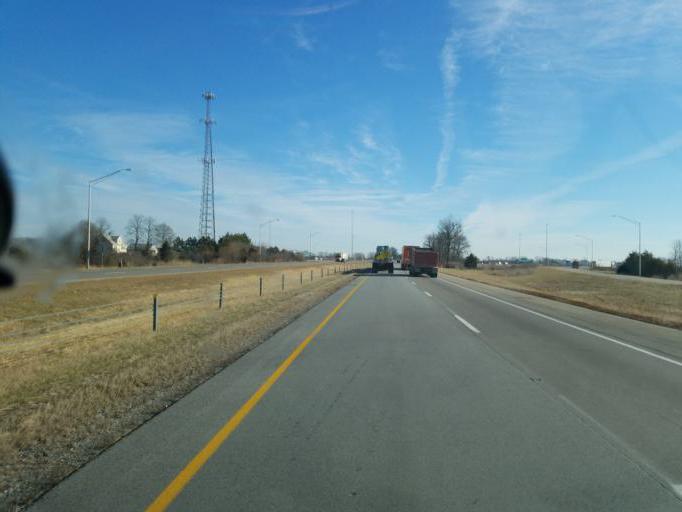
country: US
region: Indiana
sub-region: Hancock County
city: Greenfield
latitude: 39.8251
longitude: -85.7109
